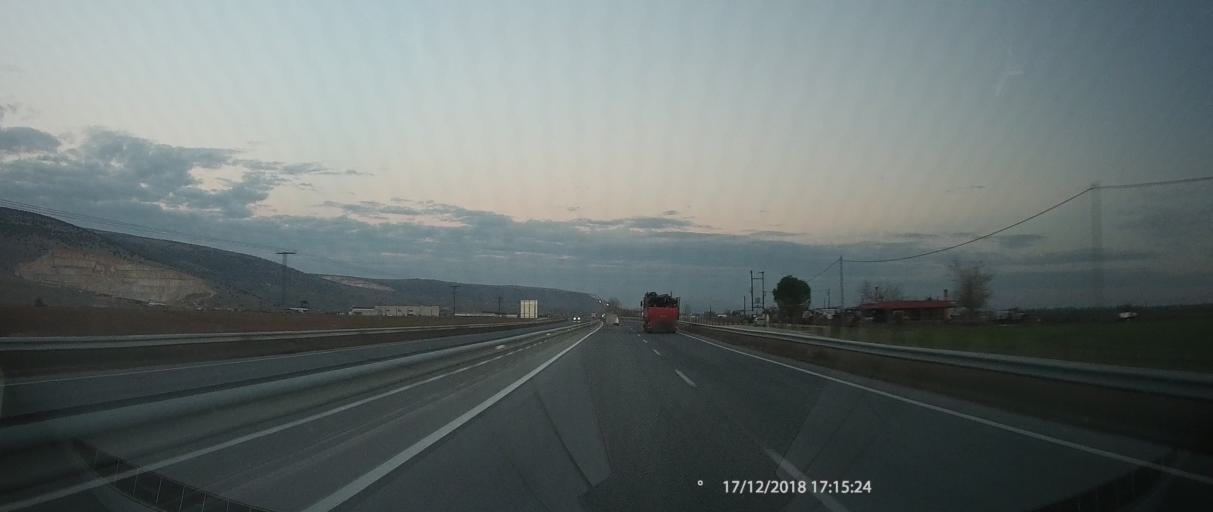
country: GR
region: Thessaly
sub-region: Trikala
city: Taxiarches
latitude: 39.5640
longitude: 21.9016
